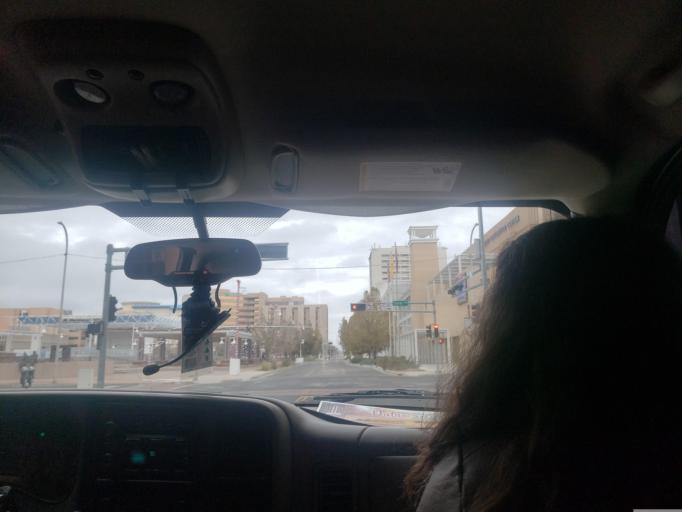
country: US
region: New Mexico
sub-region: Bernalillo County
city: Albuquerque
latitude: 35.0861
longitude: -106.6502
